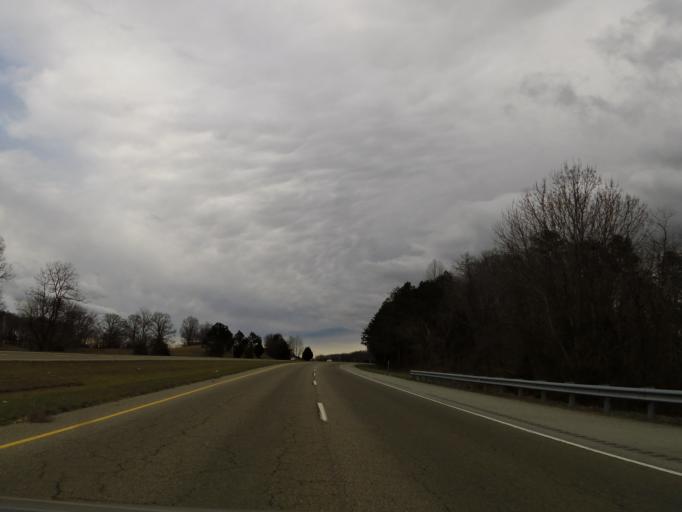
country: US
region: Tennessee
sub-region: Greene County
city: Tusculum
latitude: 36.2298
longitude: -82.6781
